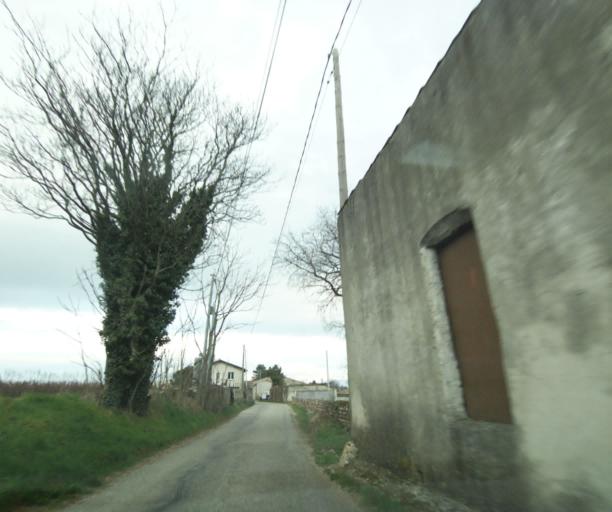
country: FR
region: Rhone-Alpes
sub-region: Departement de la Drome
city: Bourg-les-Valence
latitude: 44.9865
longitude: 4.9117
